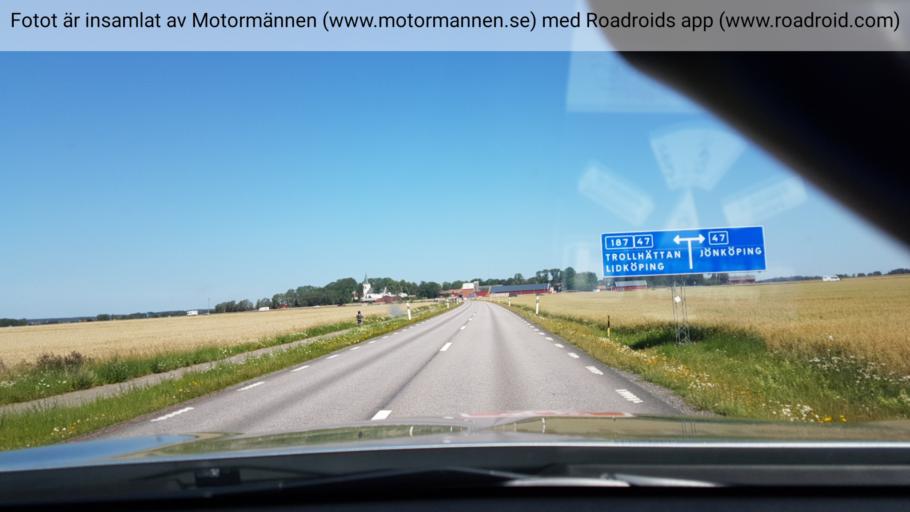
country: SE
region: Vaestra Goetaland
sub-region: Vara Kommun
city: Vara
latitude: 58.2908
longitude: 12.9609
